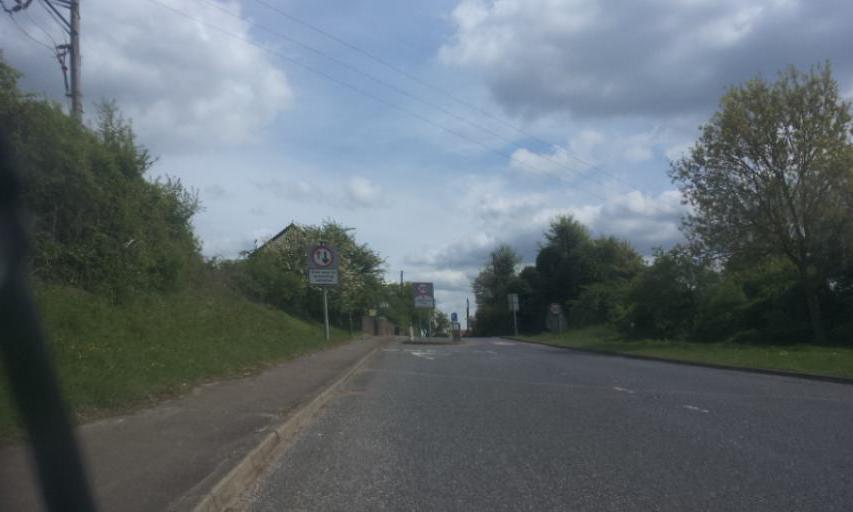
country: GB
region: England
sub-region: Kent
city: Longfield
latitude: 51.3899
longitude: 0.3298
